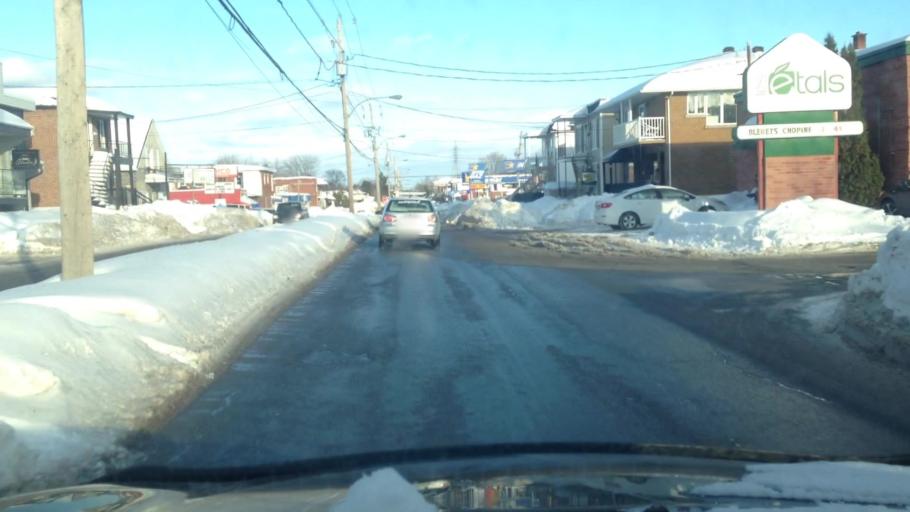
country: CA
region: Quebec
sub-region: Laurentides
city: Saint-Jerome
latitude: 45.7942
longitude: -74.0078
